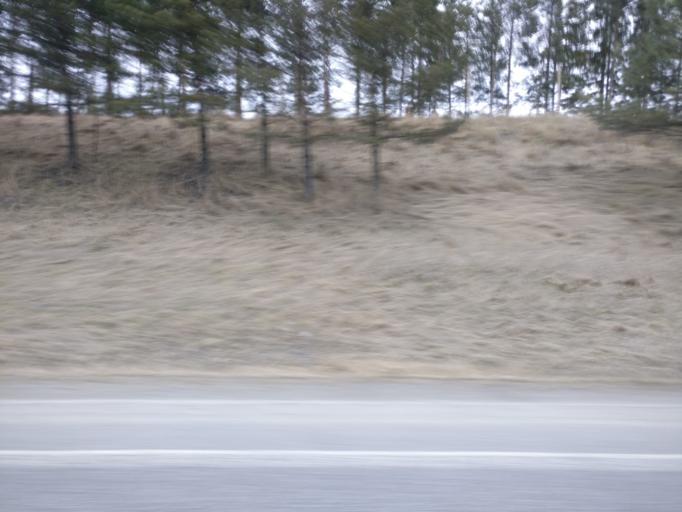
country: FI
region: Pirkanmaa
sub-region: Tampere
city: Tampere
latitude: 61.4607
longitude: 23.7869
